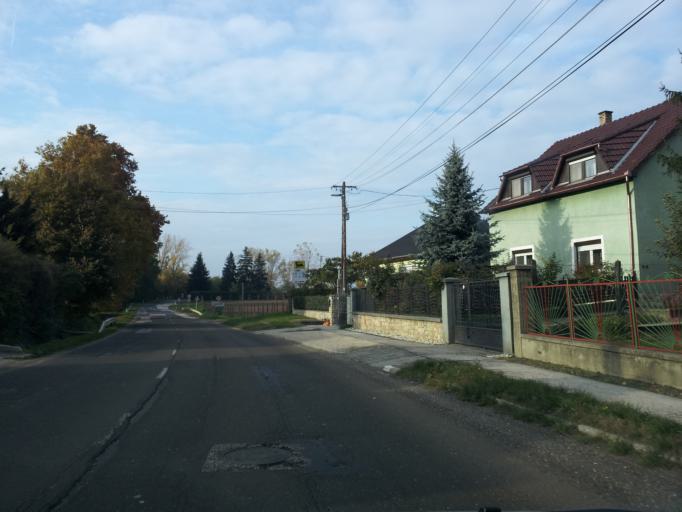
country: HU
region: Gyor-Moson-Sopron
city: Pannonhalma
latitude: 47.5253
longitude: 17.7468
